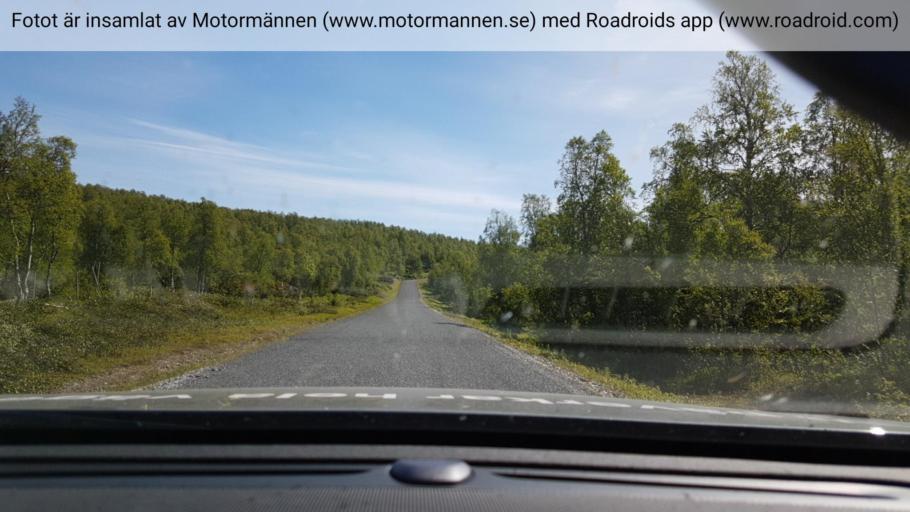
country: NO
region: Nordland
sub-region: Hattfjelldal
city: Hattfjelldal
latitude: 65.4229
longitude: 14.6635
